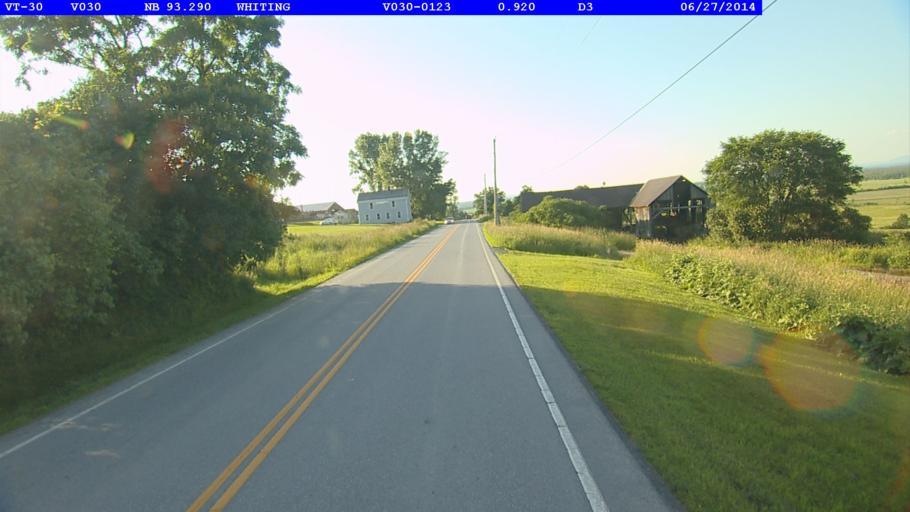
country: US
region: Vermont
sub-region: Rutland County
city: Brandon
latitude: 43.8511
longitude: -73.1994
